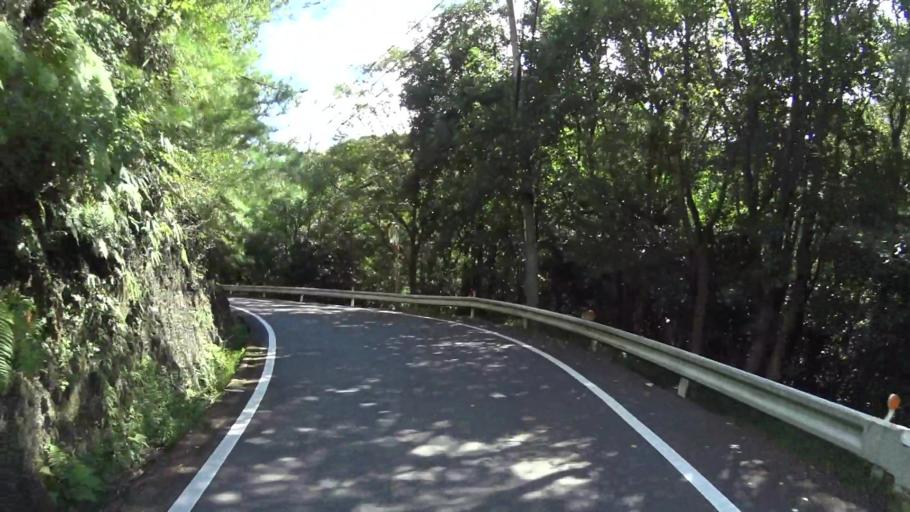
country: JP
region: Kyoto
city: Uji
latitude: 34.9111
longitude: 135.8526
